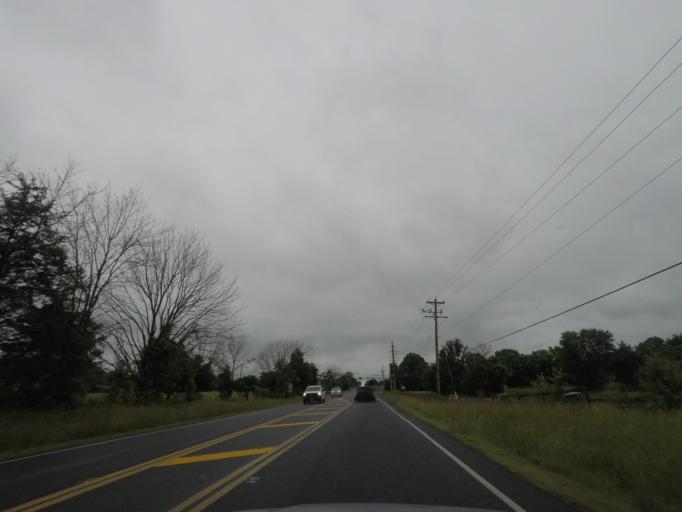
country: US
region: Virginia
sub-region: Prince William County
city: Bull Run Mountain Estates
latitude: 38.8994
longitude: -77.6305
